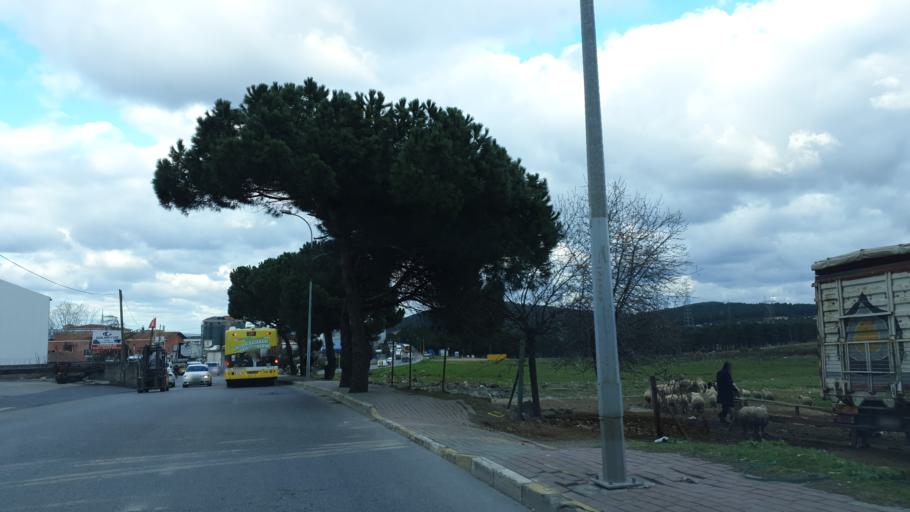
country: TR
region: Istanbul
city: Sultanbeyli
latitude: 40.9431
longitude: 29.3033
